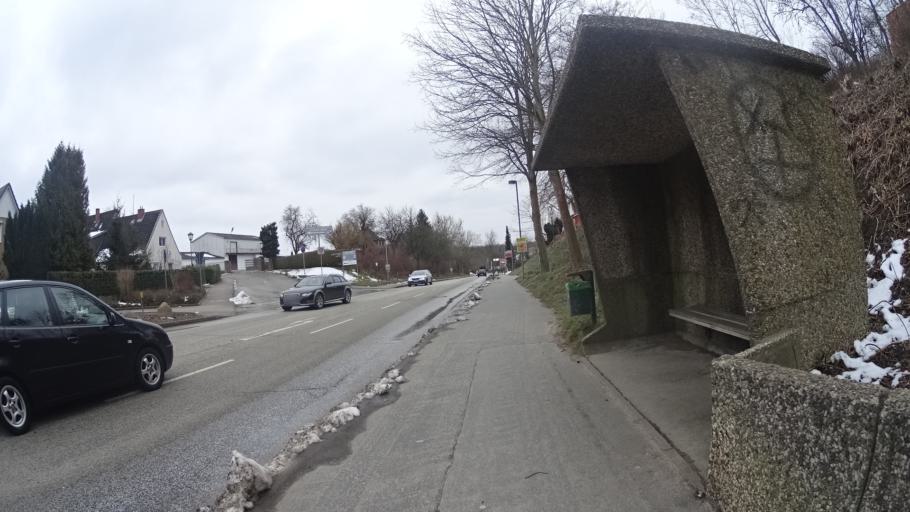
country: DE
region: Schleswig-Holstein
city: Lutjenburg
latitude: 54.2873
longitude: 10.5827
